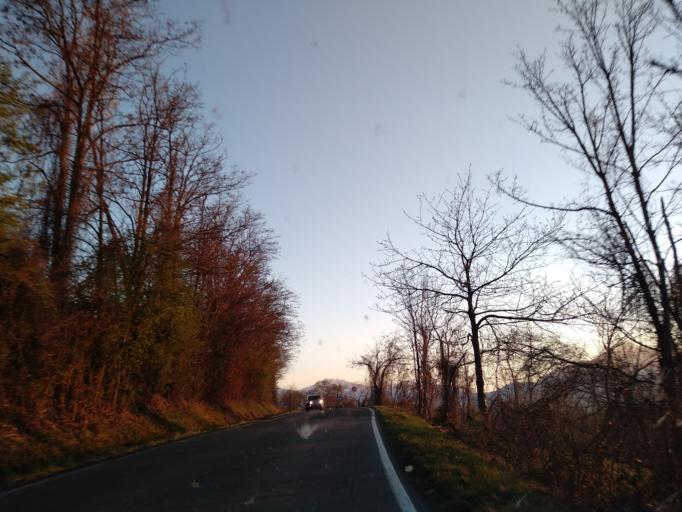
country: IT
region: Emilia-Romagna
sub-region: Provincia di Reggio Emilia
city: Castelnovo ne'Monti
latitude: 44.4235
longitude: 10.4048
